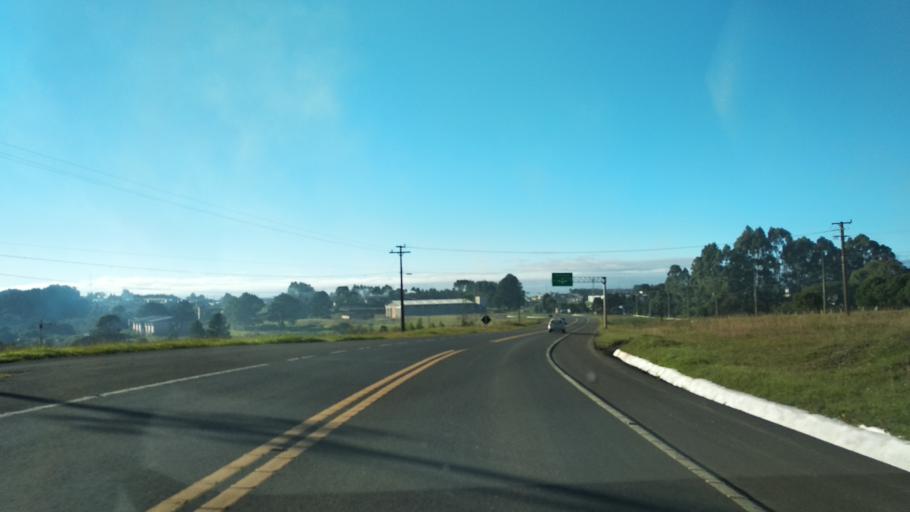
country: BR
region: Santa Catarina
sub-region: Lages
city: Lages
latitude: -27.7932
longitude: -50.3721
